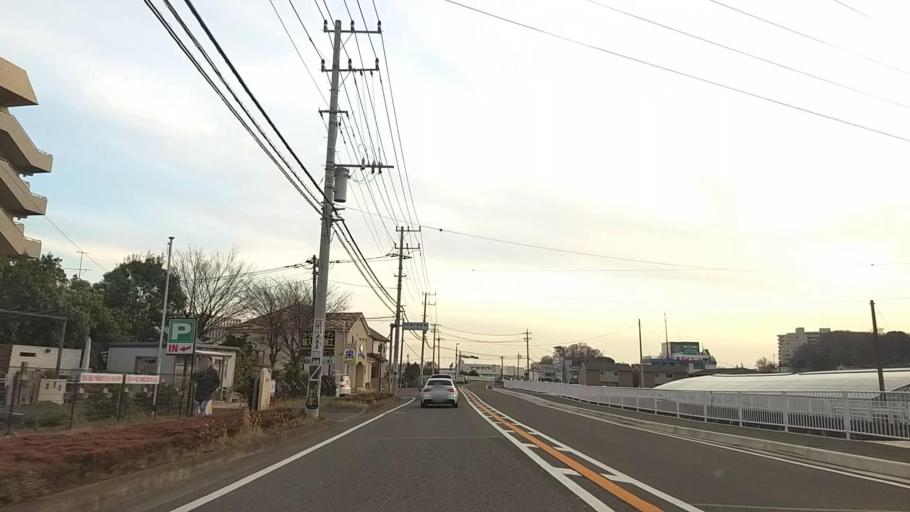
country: JP
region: Kanagawa
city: Atsugi
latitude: 35.4330
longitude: 139.3526
